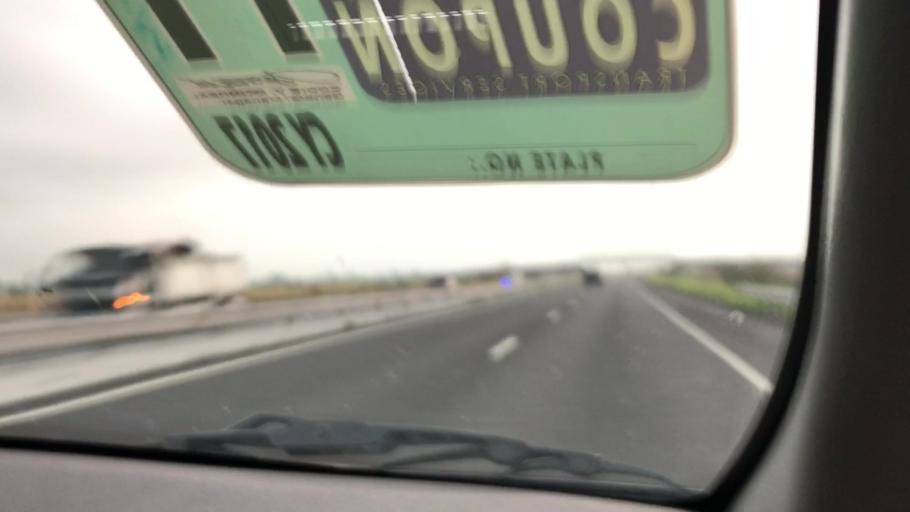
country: PH
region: Central Luzon
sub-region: Province of Tarlac
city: Mapalacsiao
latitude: 15.4188
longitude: 120.6611
